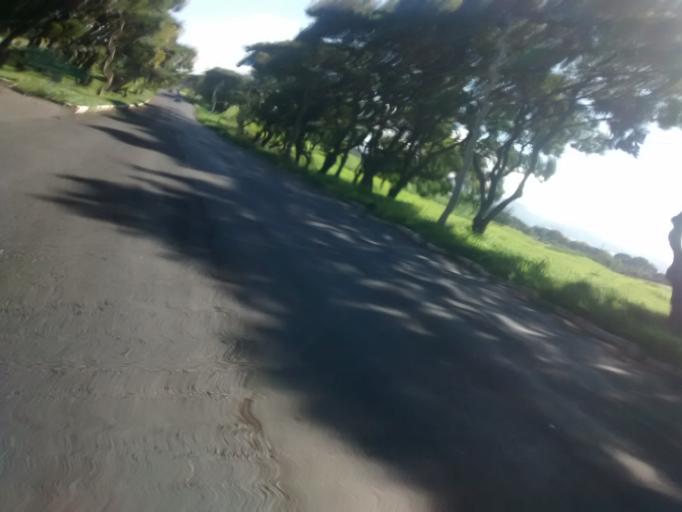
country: BR
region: Federal District
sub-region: Brasilia
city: Brasilia
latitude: -15.7794
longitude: -47.8687
